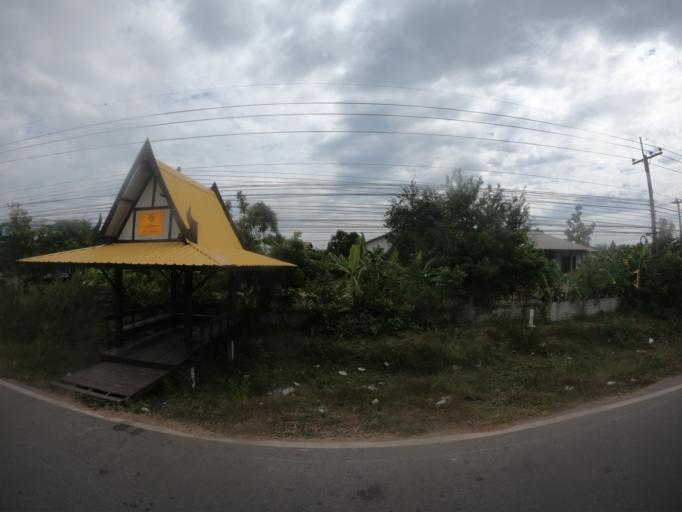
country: TH
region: Maha Sarakham
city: Kantharawichai
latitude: 16.3005
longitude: 103.2978
